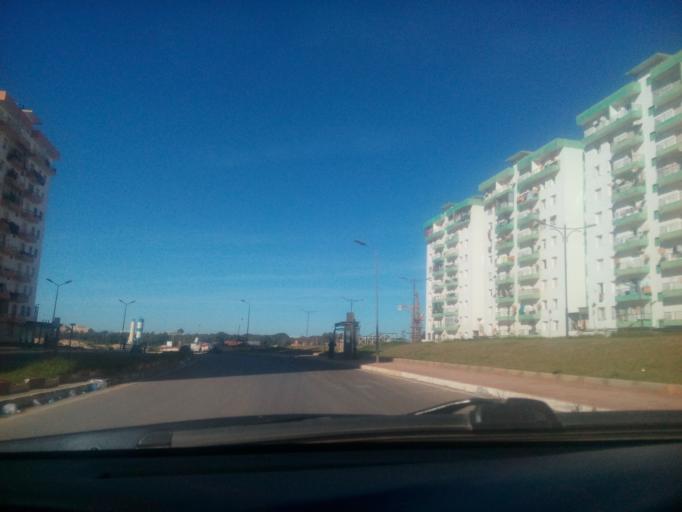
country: DZ
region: Oran
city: Bir el Djir
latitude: 35.7535
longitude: -0.5555
